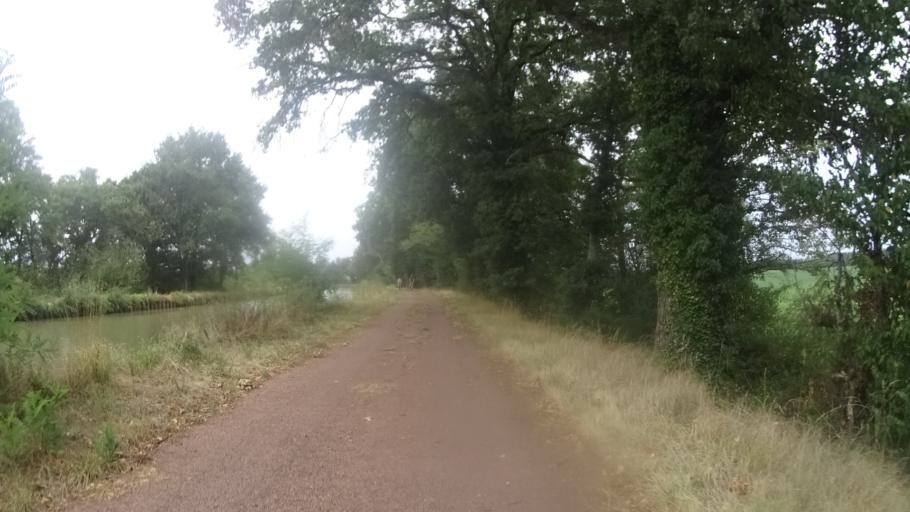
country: FR
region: Bourgogne
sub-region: Departement de la Nievre
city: Imphy
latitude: 46.8624
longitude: 3.2878
